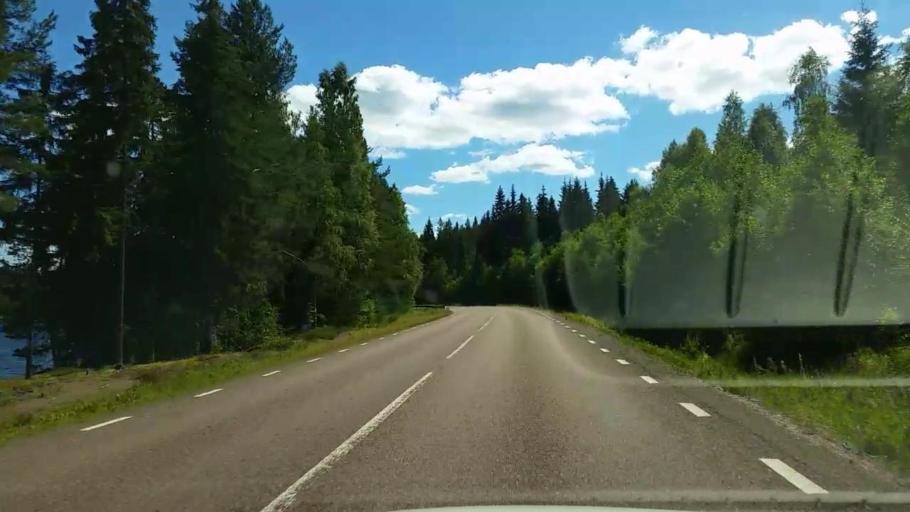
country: SE
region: Dalarna
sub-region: Faluns Kommun
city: Svardsjo
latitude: 60.9593
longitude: 15.6917
